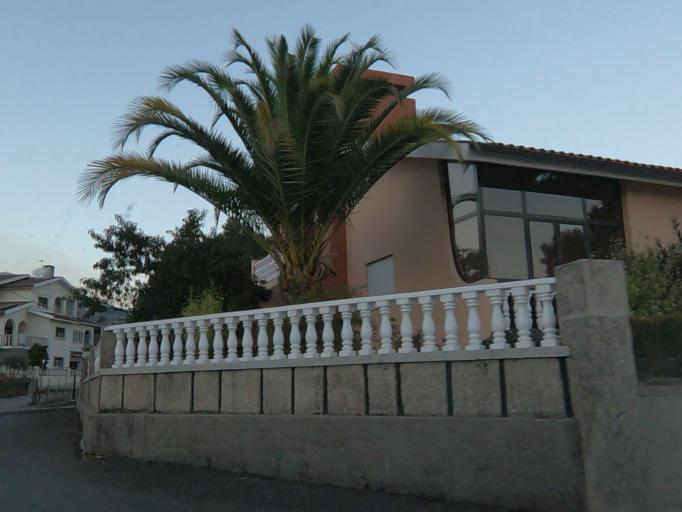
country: PT
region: Vila Real
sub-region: Vila Real
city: Vila Real
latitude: 41.3096
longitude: -7.7646
